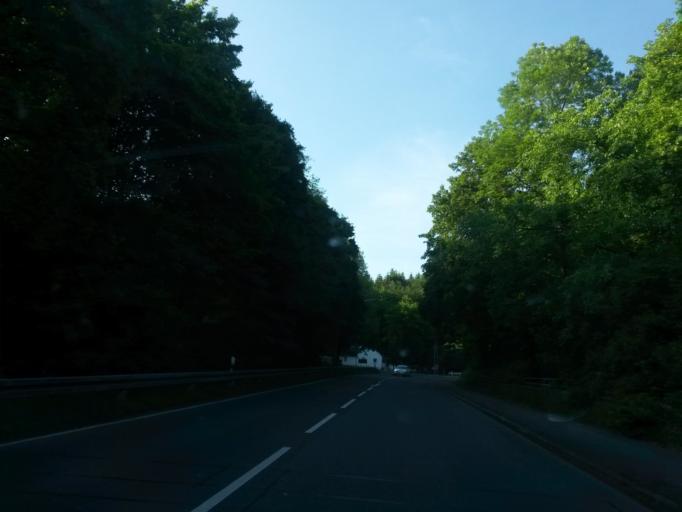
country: DE
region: North Rhine-Westphalia
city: Bergneustadt
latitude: 51.0239
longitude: 7.6830
